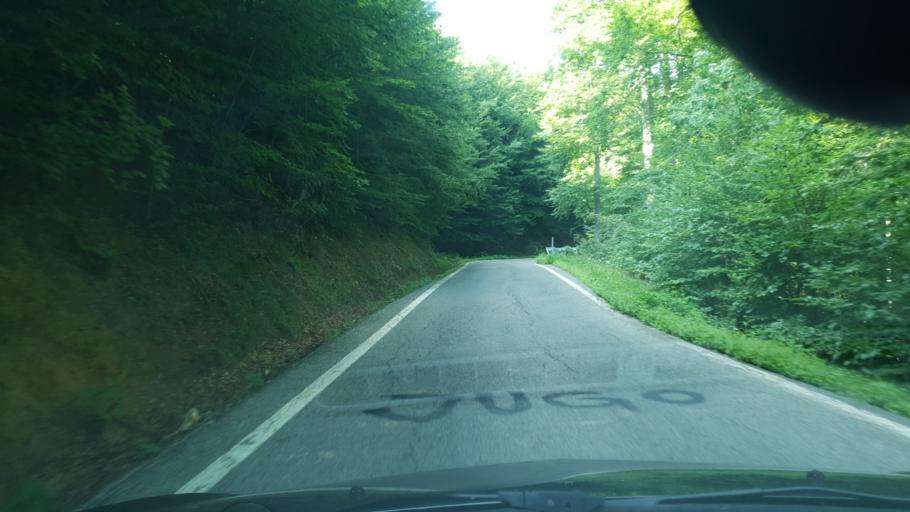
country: HR
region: Grad Zagreb
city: Kasina
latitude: 45.8800
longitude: 15.9747
